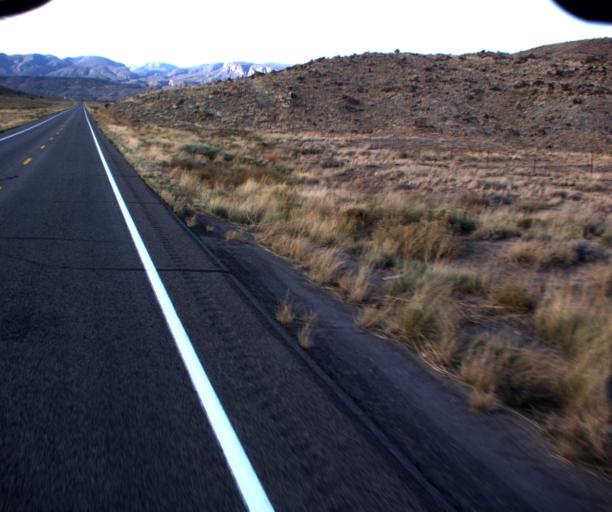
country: US
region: New Mexico
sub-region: San Juan County
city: Shiprock
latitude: 36.9396
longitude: -109.0763
